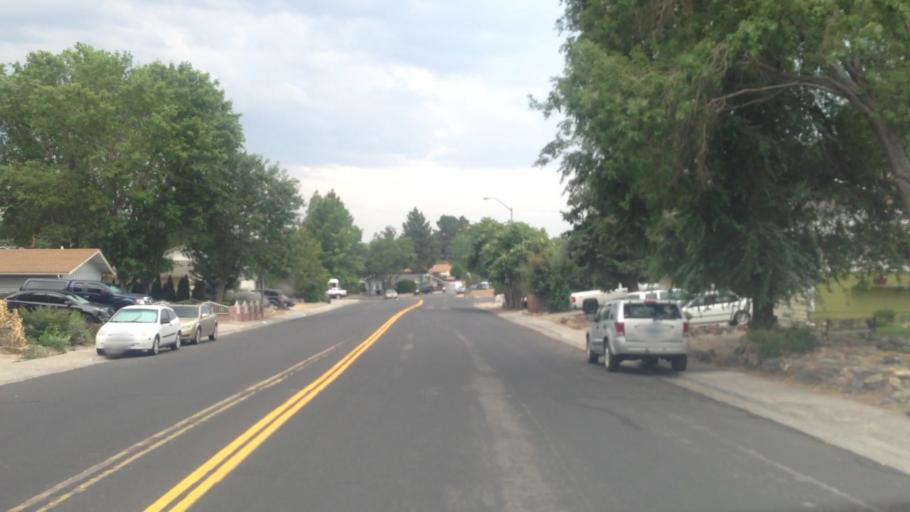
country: US
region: Nevada
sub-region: Washoe County
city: Reno
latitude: 39.5364
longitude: -119.8339
